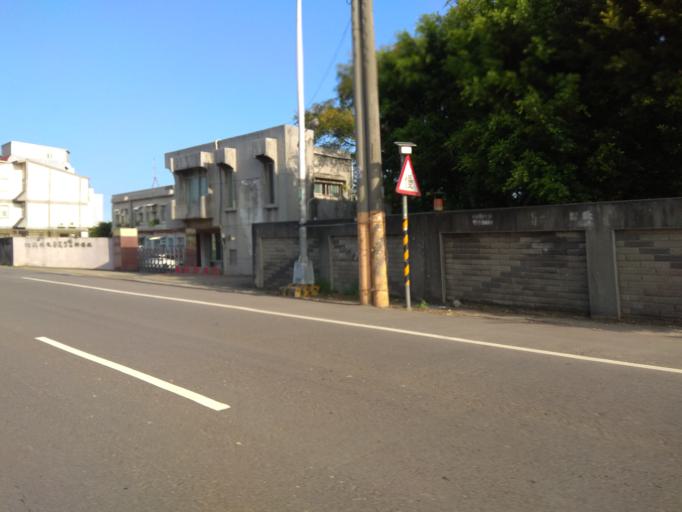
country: TW
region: Taiwan
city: Taoyuan City
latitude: 24.9683
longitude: 121.1388
